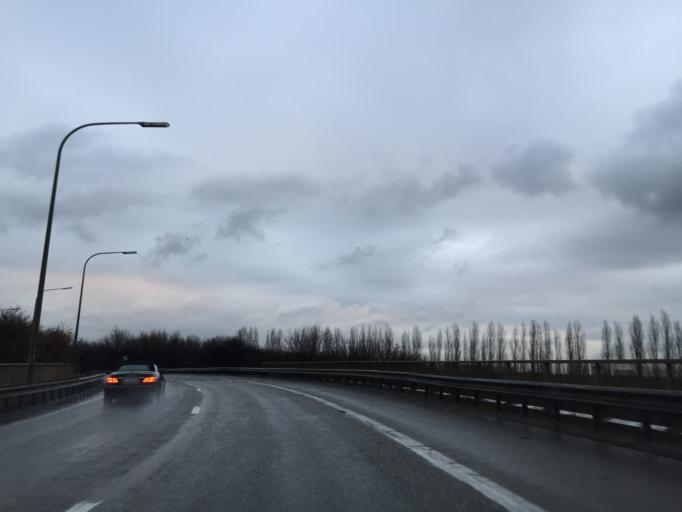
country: BE
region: Flanders
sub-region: Provincie Antwerpen
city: Antwerpen
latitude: 51.2693
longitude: 4.4080
